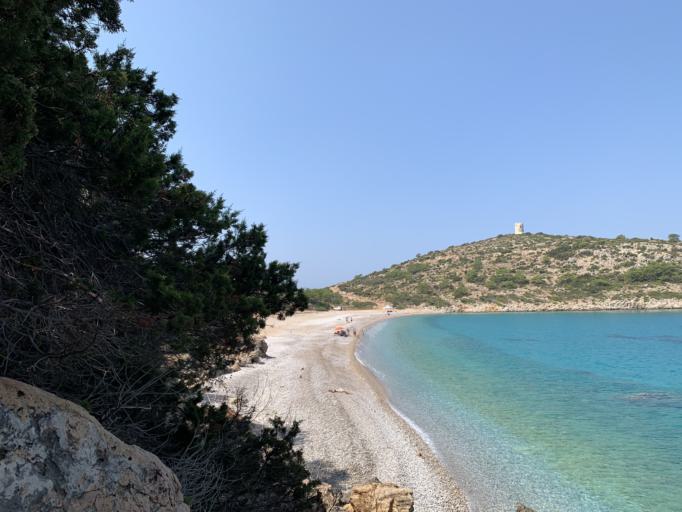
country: GR
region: North Aegean
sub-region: Chios
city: Chios
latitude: 38.3647
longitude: 25.9932
